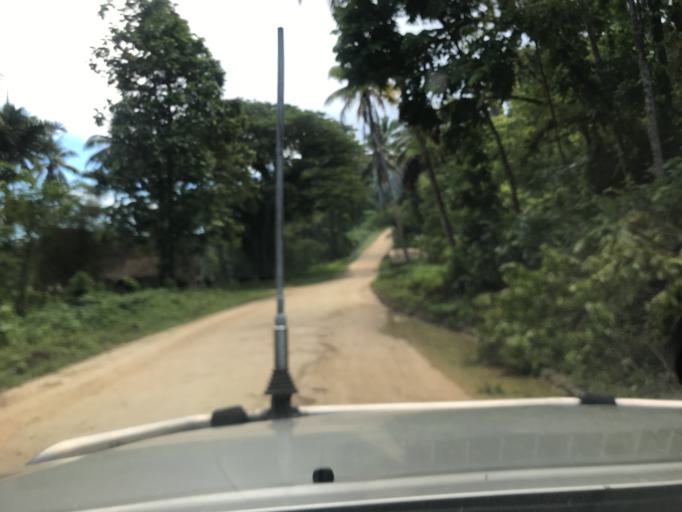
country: SB
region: Malaita
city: Auki
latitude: -8.6392
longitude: 160.6658
